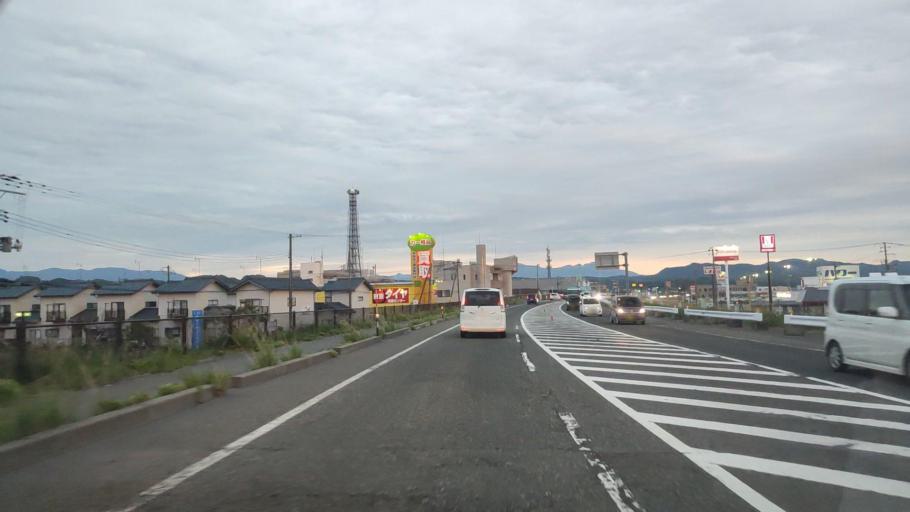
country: JP
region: Niigata
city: Niitsu-honcho
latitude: 37.7929
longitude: 139.1105
